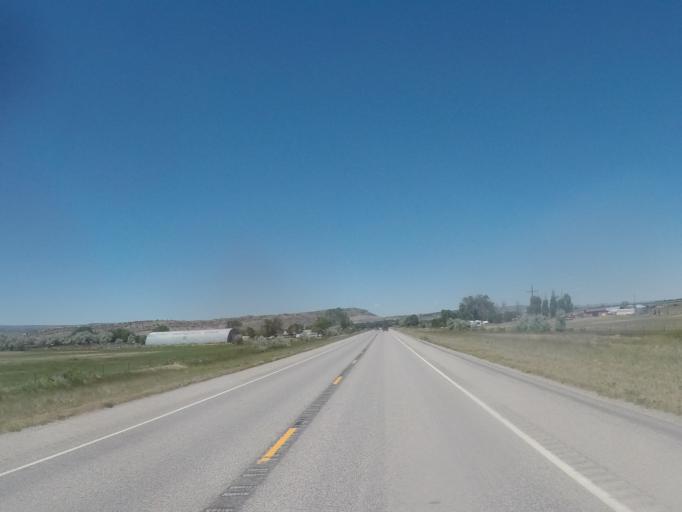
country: US
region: Montana
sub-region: Carbon County
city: Red Lodge
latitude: 45.2436
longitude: -108.8993
